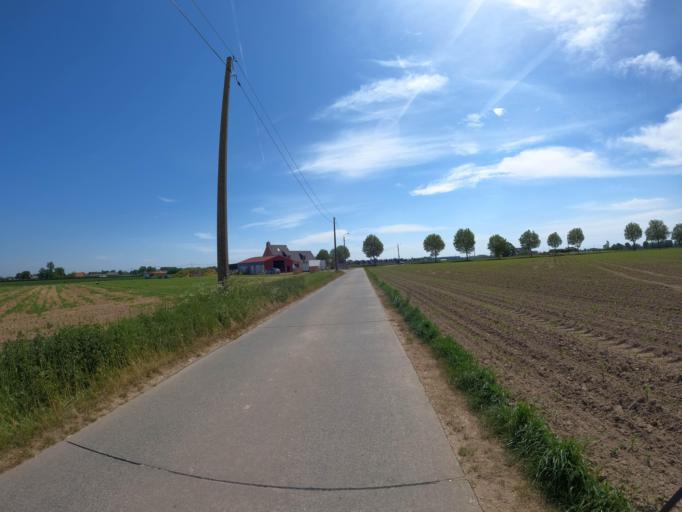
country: BE
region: Flanders
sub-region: Provincie West-Vlaanderen
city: Dentergem
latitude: 51.0105
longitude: 3.4633
